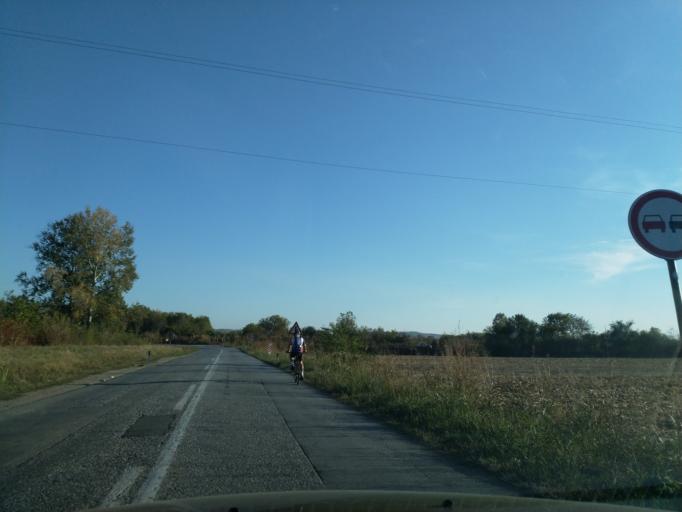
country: RS
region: Central Serbia
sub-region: Pomoravski Okrug
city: Svilajnac
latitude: 44.2243
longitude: 21.1484
